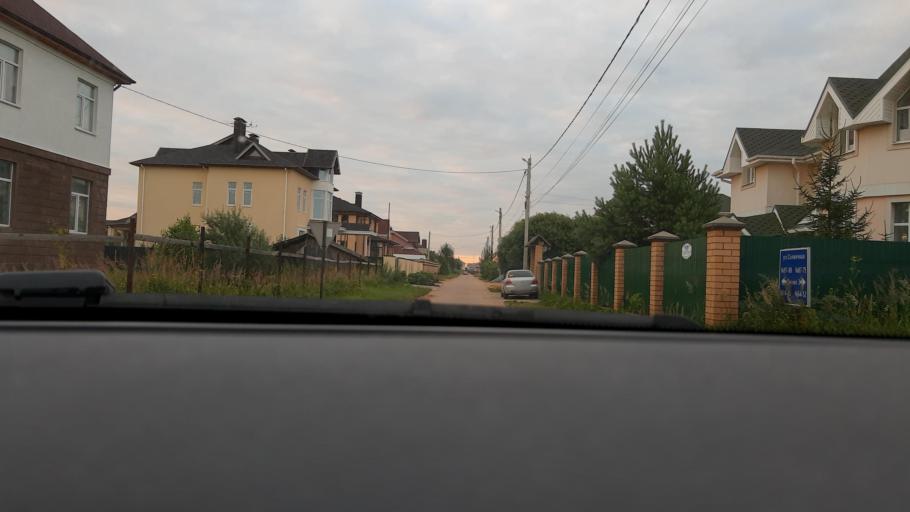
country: RU
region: Nizjnij Novgorod
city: Burevestnik
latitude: 56.1943
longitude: 43.8646
